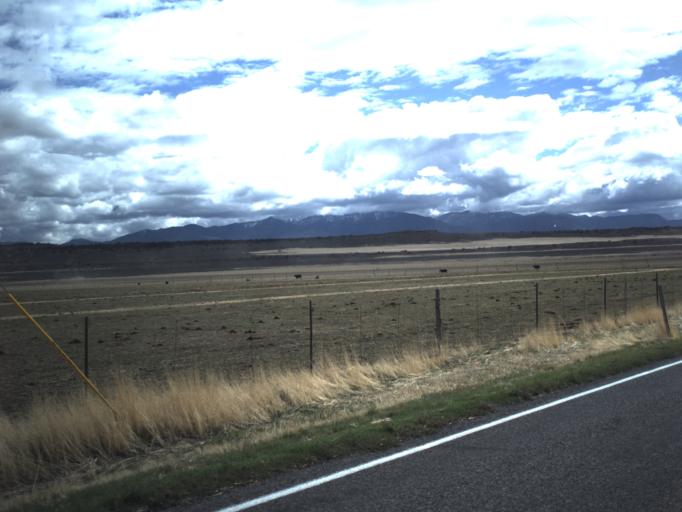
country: US
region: Utah
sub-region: Millard County
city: Fillmore
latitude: 39.0322
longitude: -112.4100
